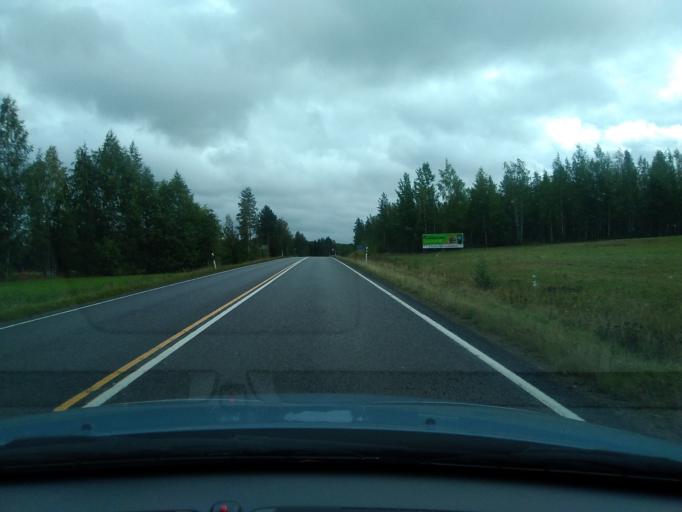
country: FI
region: Central Finland
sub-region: Saarijaervi-Viitasaari
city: Saarijaervi
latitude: 62.6863
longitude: 25.3382
